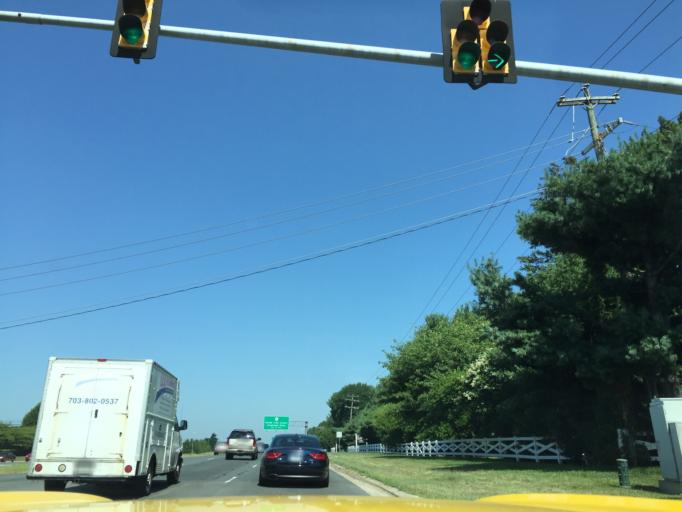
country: US
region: Virginia
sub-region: Loudoun County
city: Dulles Town Center
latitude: 39.0376
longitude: -77.4151
